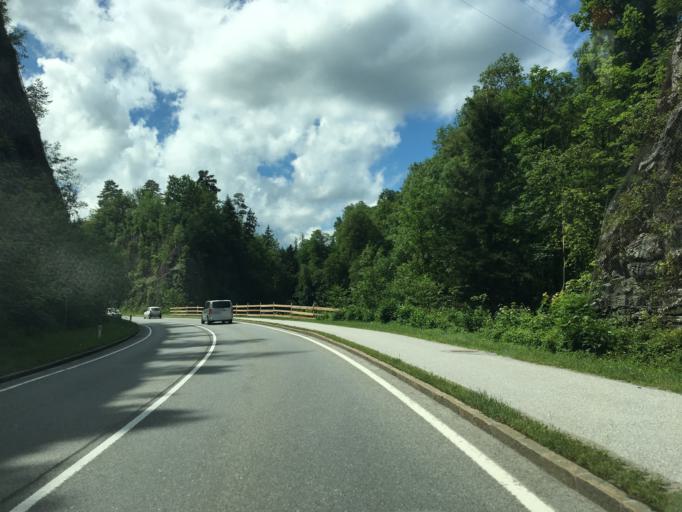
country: AT
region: Salzburg
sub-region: Politischer Bezirk Hallein
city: Oberalm
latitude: 47.7006
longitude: 13.1145
